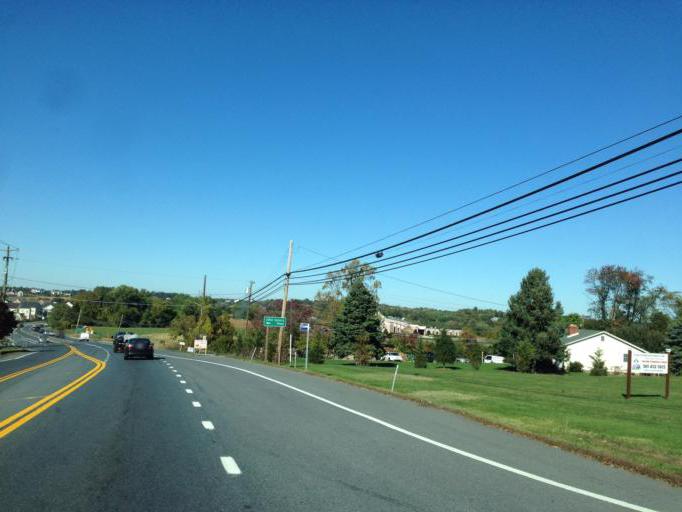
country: US
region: Maryland
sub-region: Montgomery County
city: Clarksburg
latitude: 39.2300
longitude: -77.2367
